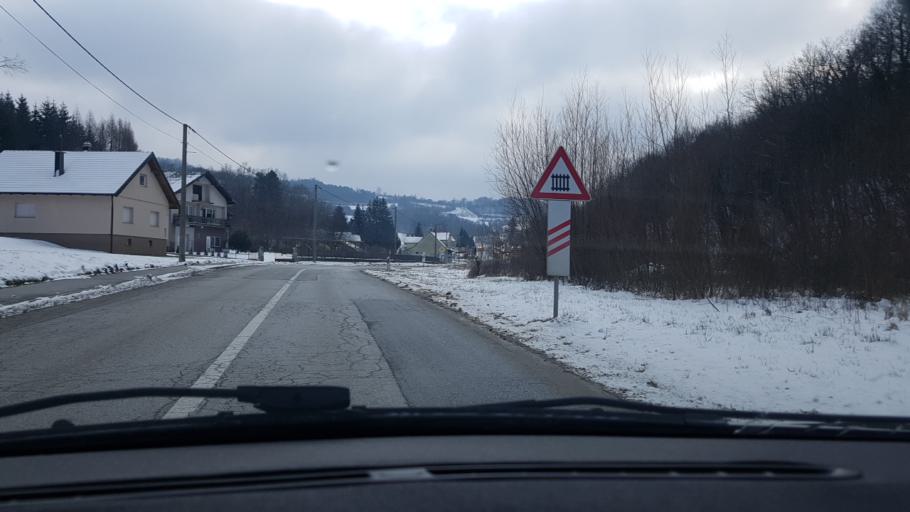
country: HR
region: Krapinsko-Zagorska
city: Mihovljan
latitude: 46.1768
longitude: 15.9834
